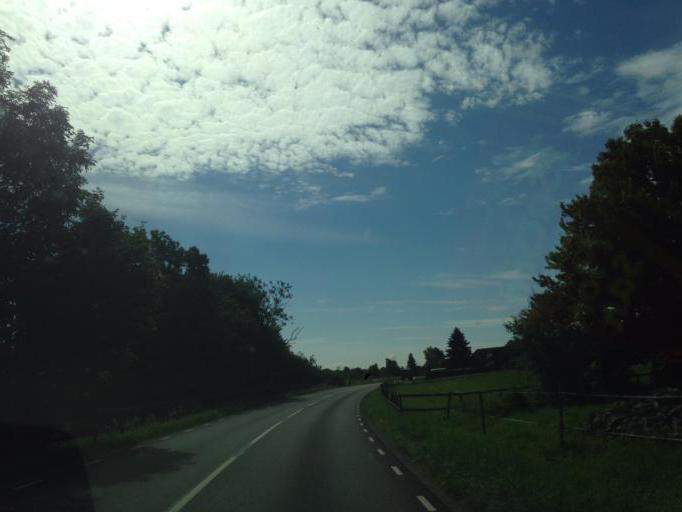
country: SE
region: Skane
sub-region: Tomelilla Kommun
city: Tomelilla
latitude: 55.6159
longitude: 13.9123
